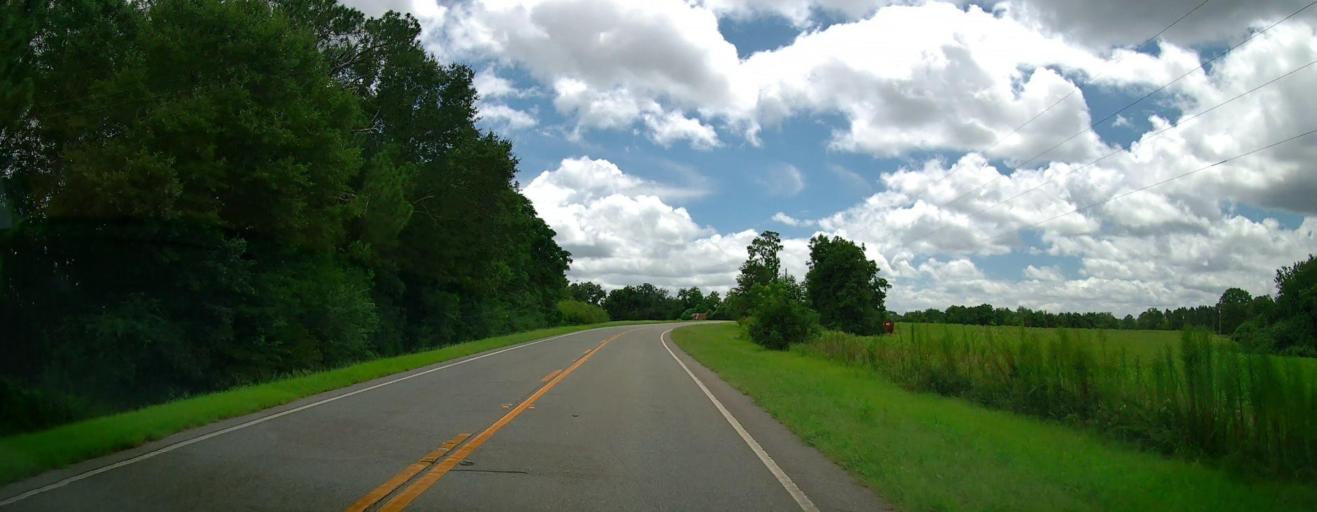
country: US
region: Georgia
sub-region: Wilcox County
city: Rochelle
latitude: 31.9607
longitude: -83.5421
